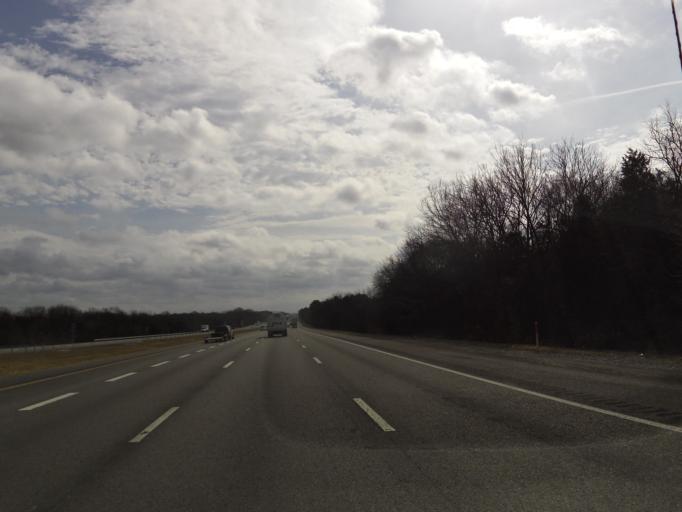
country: US
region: Tennessee
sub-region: Rutherford County
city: Smyrna
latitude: 35.9189
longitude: -86.5148
